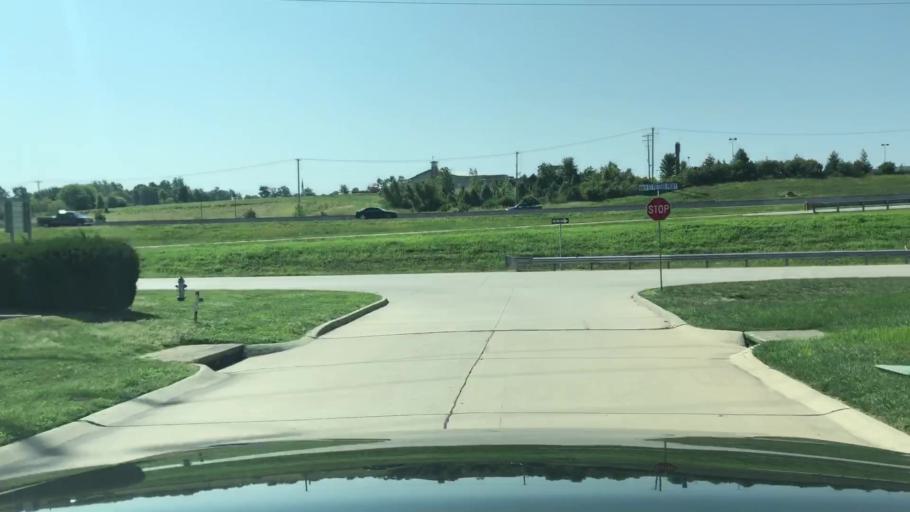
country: US
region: Missouri
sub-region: Saint Charles County
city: Saint Peters
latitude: 38.7487
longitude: -90.5879
